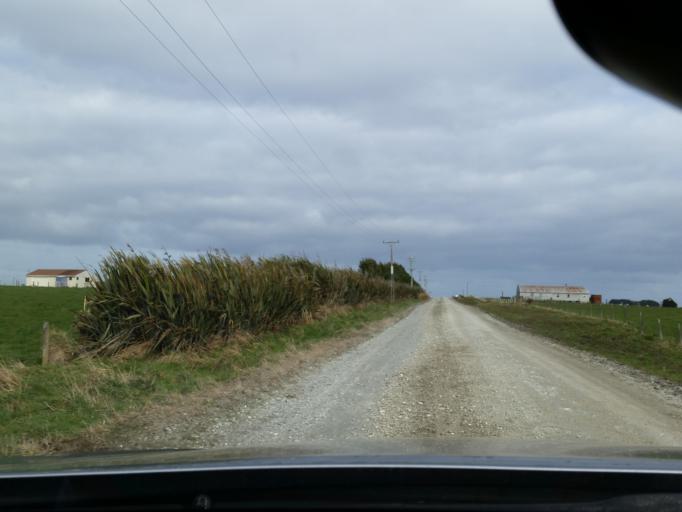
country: NZ
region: Southland
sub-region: Invercargill City
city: Invercargill
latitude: -46.4474
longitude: 168.5062
